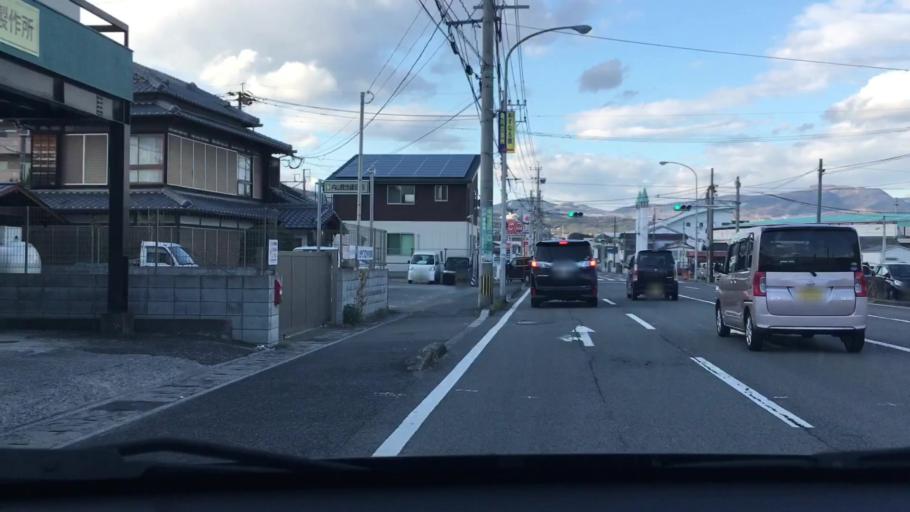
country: JP
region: Oita
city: Beppu
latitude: 33.3199
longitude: 131.4988
